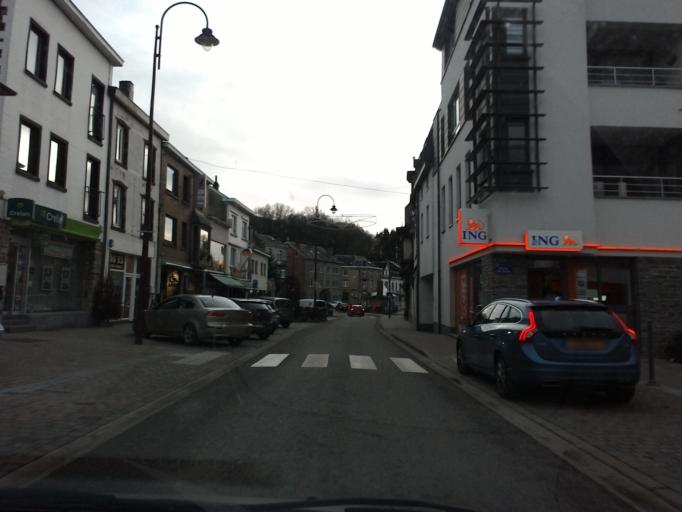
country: BE
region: Wallonia
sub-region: Province du Luxembourg
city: Vielsalm
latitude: 50.2847
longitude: 5.9148
